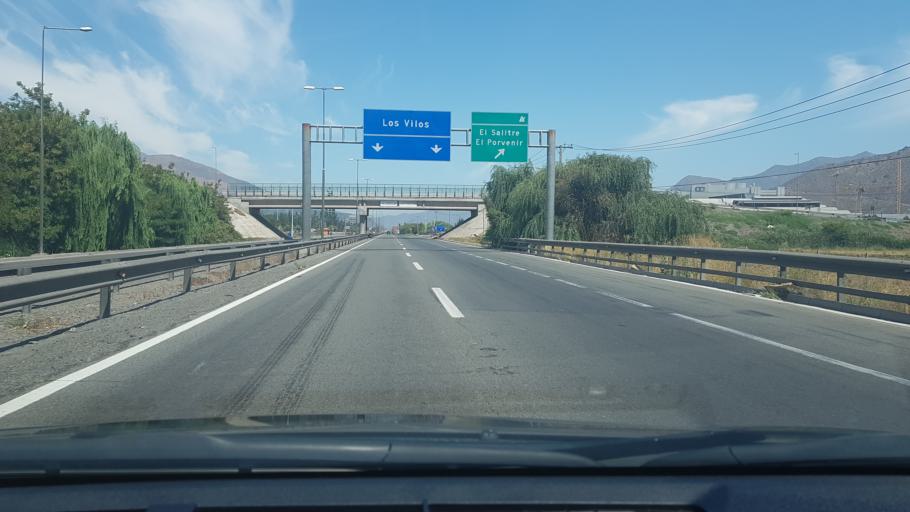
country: CL
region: Valparaiso
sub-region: Provincia de San Felipe
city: Llaillay
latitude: -32.8511
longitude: -70.9415
